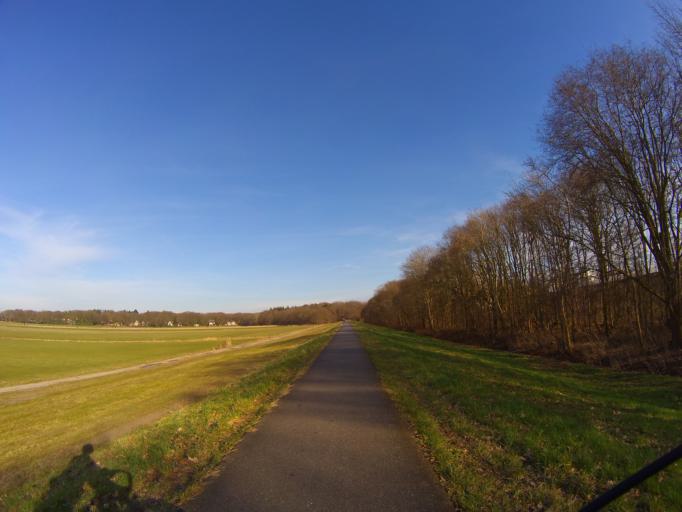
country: NL
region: North Holland
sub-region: Gemeente Naarden
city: Naarden
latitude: 52.2970
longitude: 5.1799
